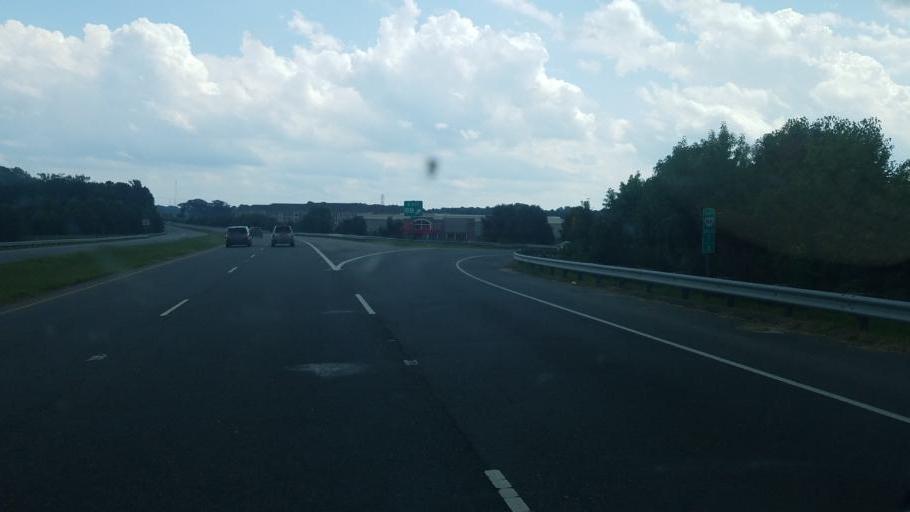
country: US
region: North Carolina
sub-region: Currituck County
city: Moyock
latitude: 36.6569
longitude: -76.2296
